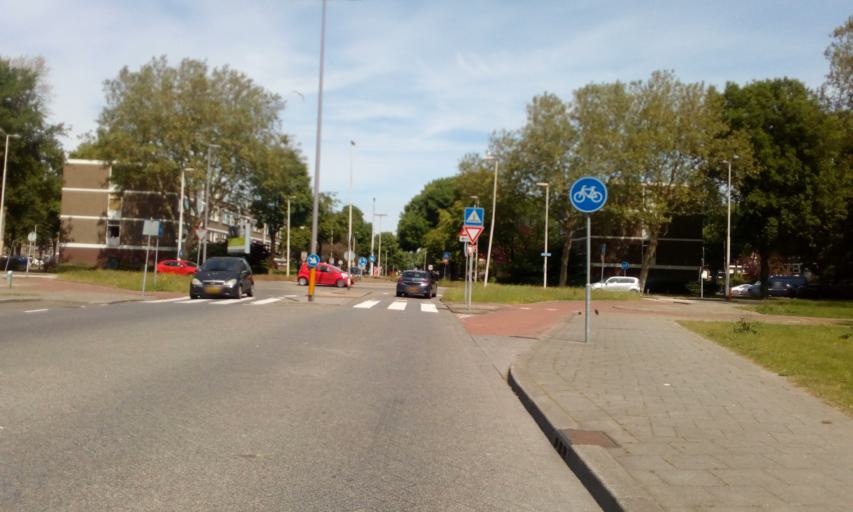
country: NL
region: South Holland
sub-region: Gemeente Rotterdam
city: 's-Gravenland
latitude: 51.9376
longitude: 4.5399
